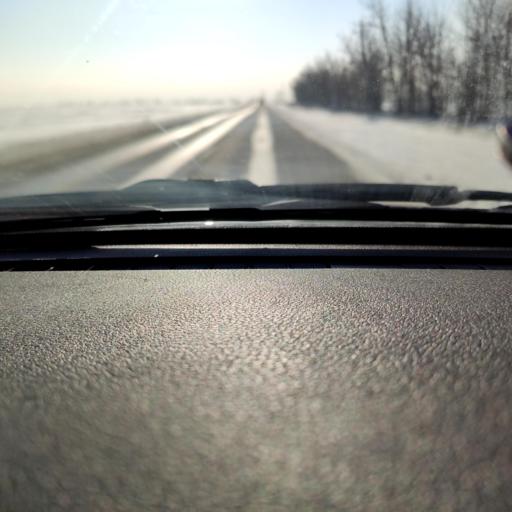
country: RU
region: Voronezj
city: Novaya Usman'
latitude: 51.5988
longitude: 39.3735
